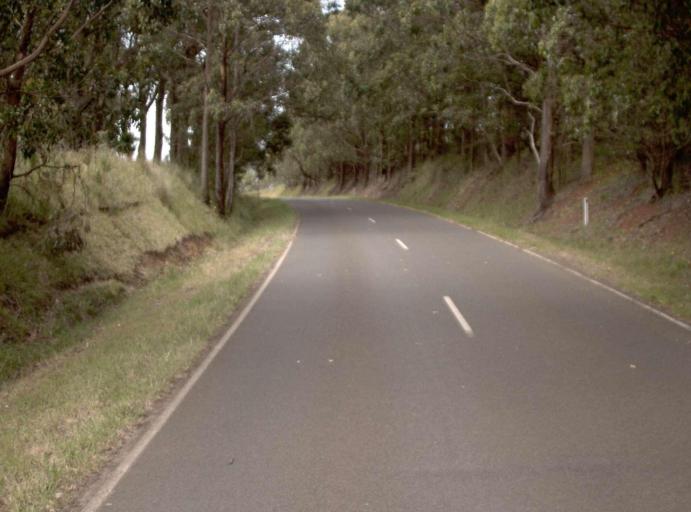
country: AU
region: Victoria
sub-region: Latrobe
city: Traralgon
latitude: -38.3570
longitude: 146.7089
